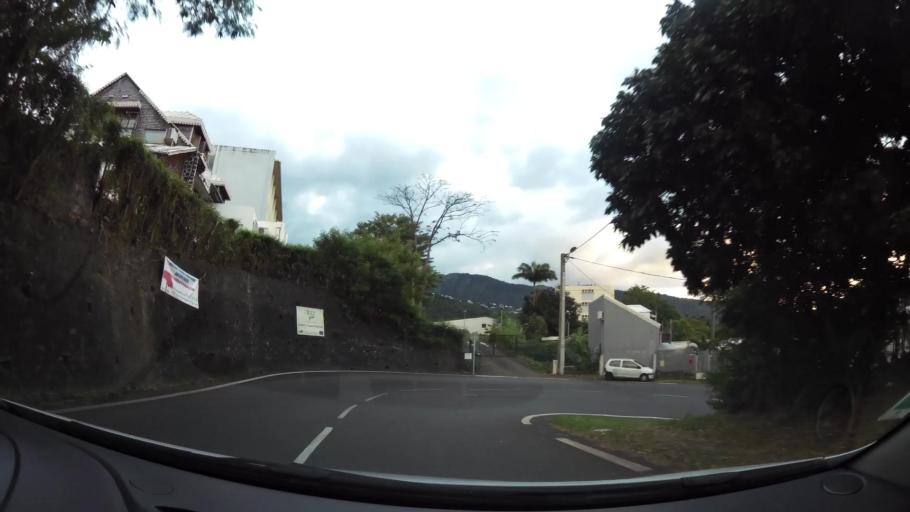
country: RE
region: Reunion
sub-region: Reunion
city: Saint-Denis
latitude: -20.9005
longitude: 55.4626
